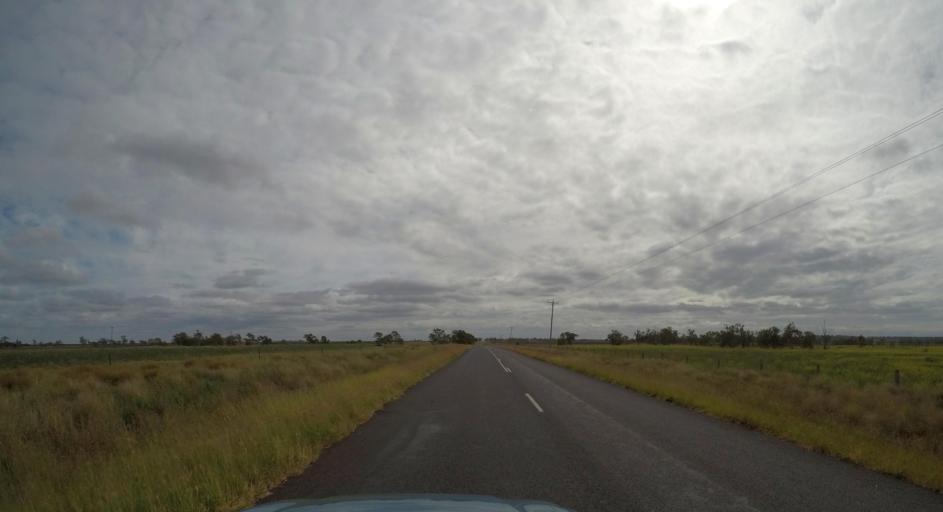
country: AU
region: Queensland
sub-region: Western Downs
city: Dalby
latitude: -26.9859
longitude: 151.2267
